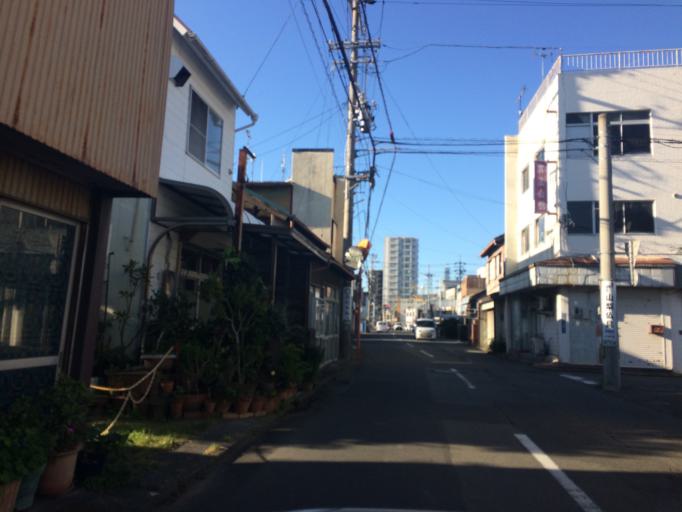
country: JP
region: Shizuoka
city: Shizuoka-shi
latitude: 34.9698
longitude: 138.3983
